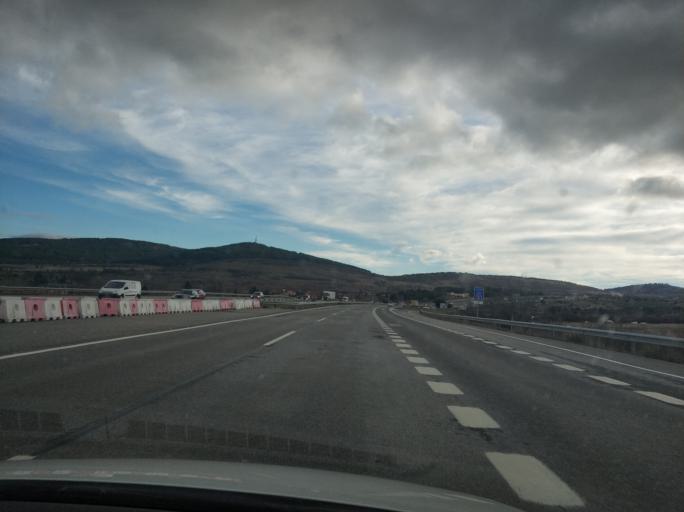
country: ES
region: Madrid
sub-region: Provincia de Madrid
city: Buitrago del Lozoya
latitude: 40.9845
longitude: -3.6403
